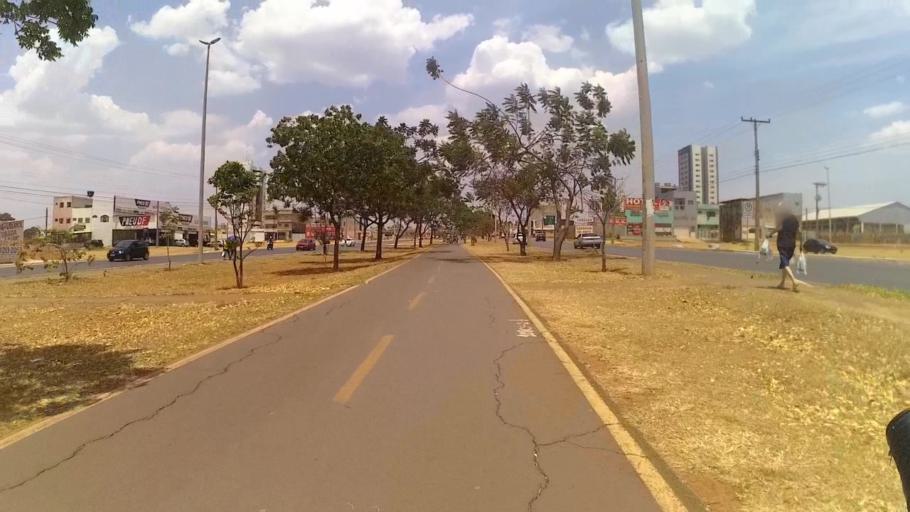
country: BR
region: Federal District
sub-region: Brasilia
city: Brasilia
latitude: -15.8735
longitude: -48.0727
